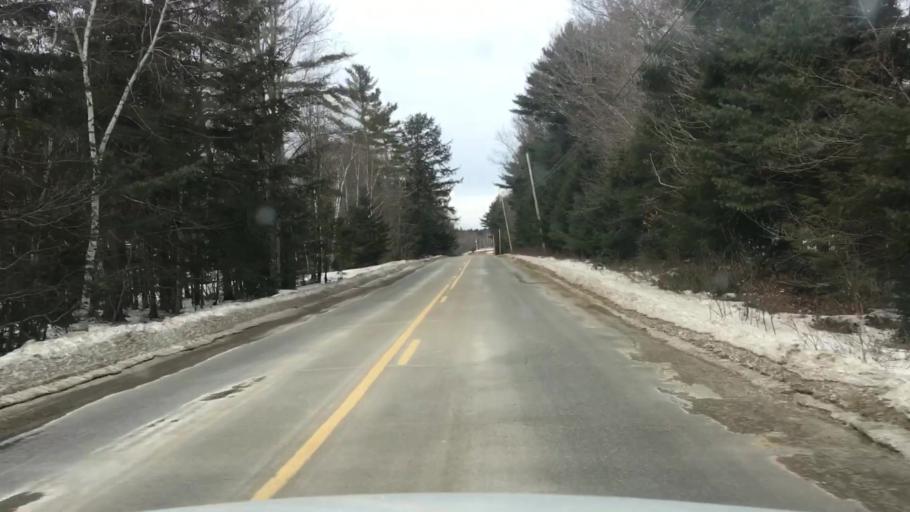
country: US
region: Maine
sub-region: Kennebec County
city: Chelsea
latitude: 44.2622
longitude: -69.6468
